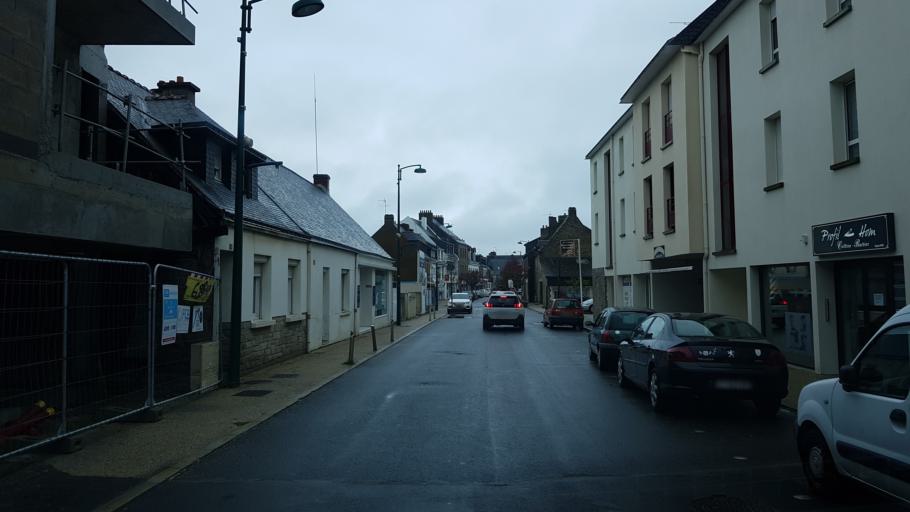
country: FR
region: Brittany
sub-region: Departement du Morbihan
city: Sarzeau
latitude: 47.5263
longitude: -2.7722
